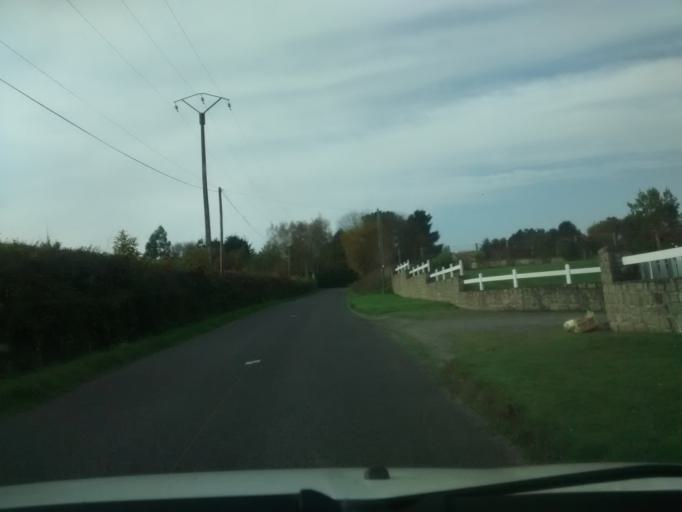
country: FR
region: Brittany
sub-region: Departement d'Ille-et-Vilaine
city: Noyal-sur-Vilaine
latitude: 48.1144
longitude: -1.5148
